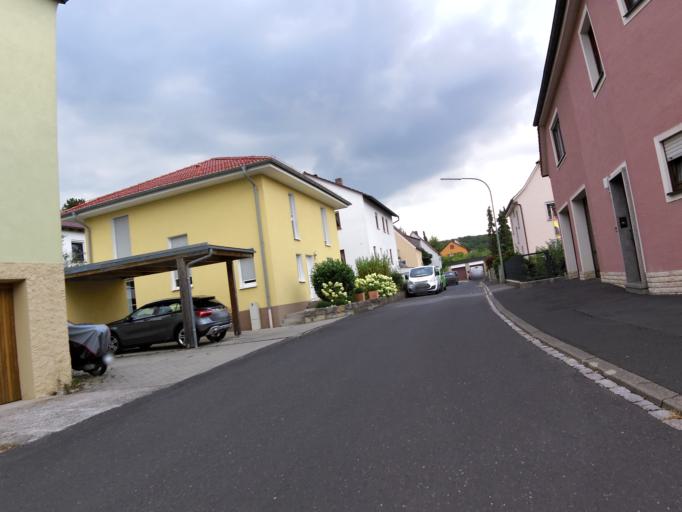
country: DE
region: Bavaria
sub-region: Regierungsbezirk Unterfranken
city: Hochberg
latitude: 49.7799
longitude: 9.8724
